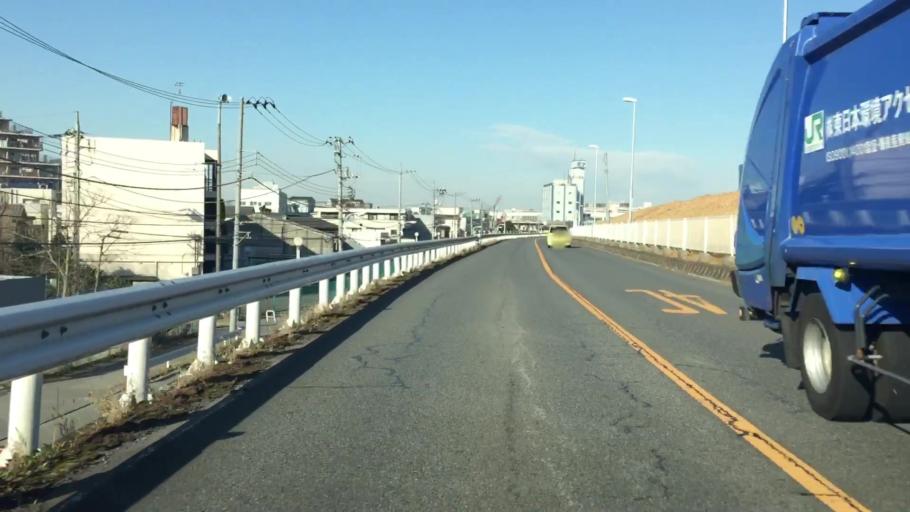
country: JP
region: Saitama
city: Kawaguchi
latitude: 35.7568
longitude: 139.7656
